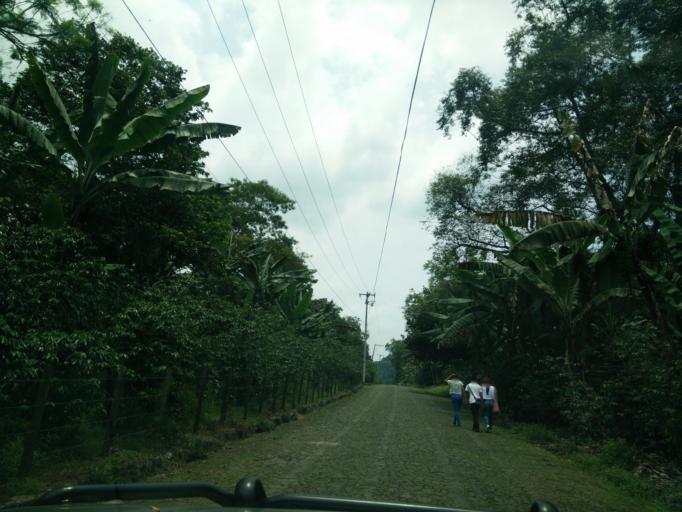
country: MX
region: Veracruz
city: Xico
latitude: 19.4044
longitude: -96.9927
